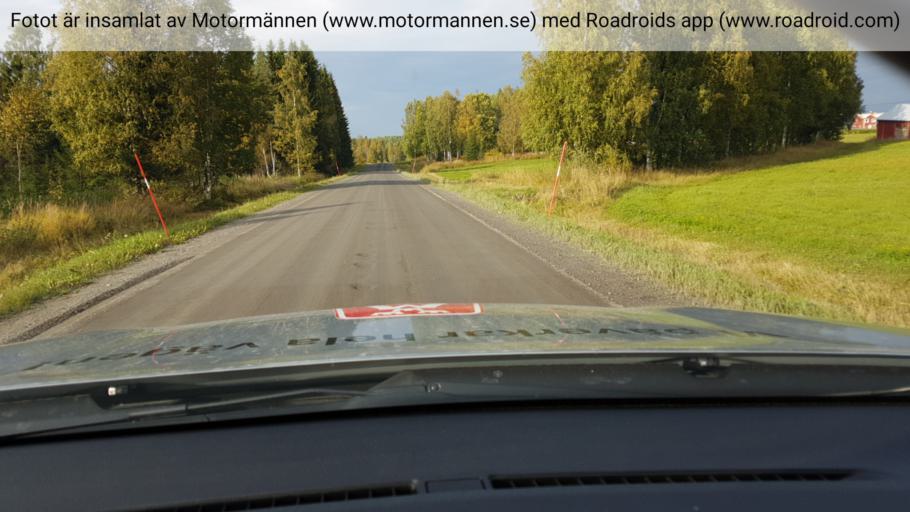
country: SE
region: Jaemtland
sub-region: Stroemsunds Kommun
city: Stroemsund
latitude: 64.0296
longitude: 15.8097
